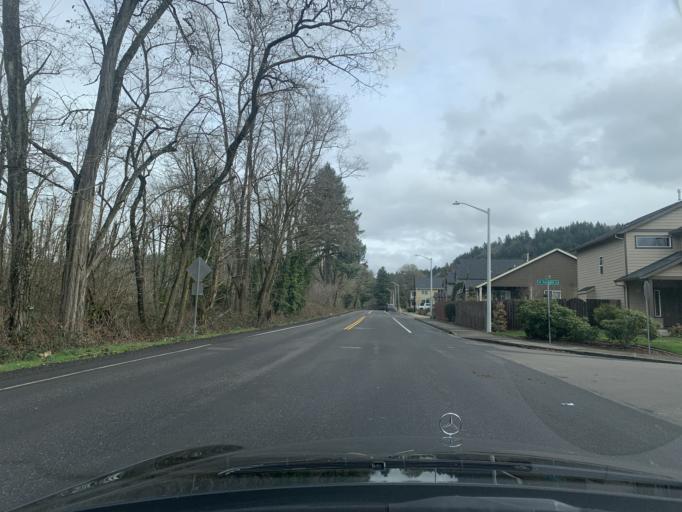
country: US
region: Oregon
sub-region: Multnomah County
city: Gresham
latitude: 45.4700
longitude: -122.4589
